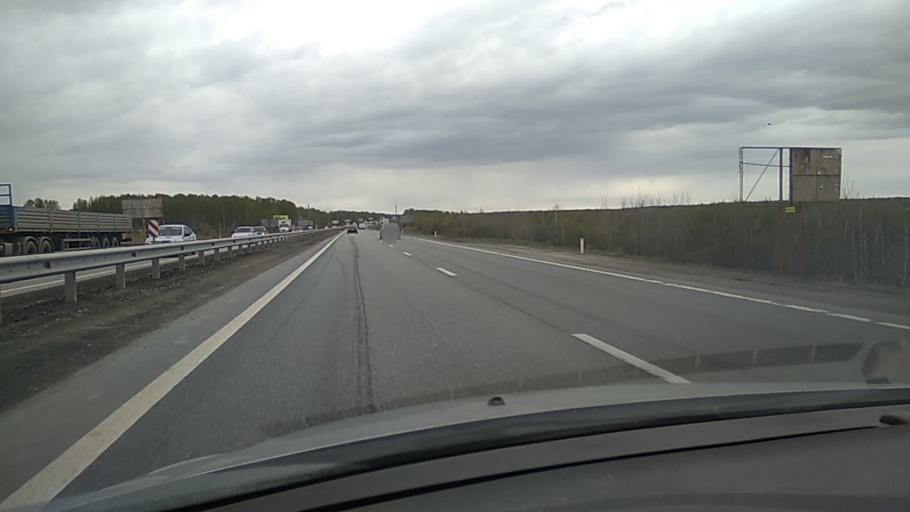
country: RU
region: Sverdlovsk
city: Bobrovskiy
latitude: 56.7567
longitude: 60.9390
